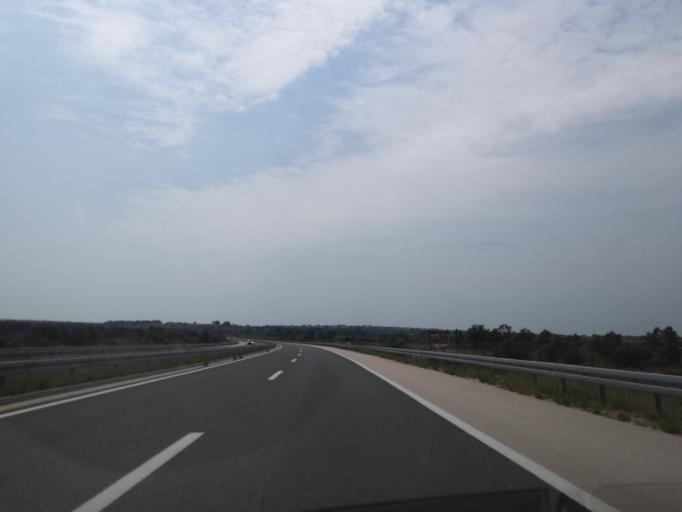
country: HR
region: Zadarska
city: Policnik
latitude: 44.1705
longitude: 15.4227
